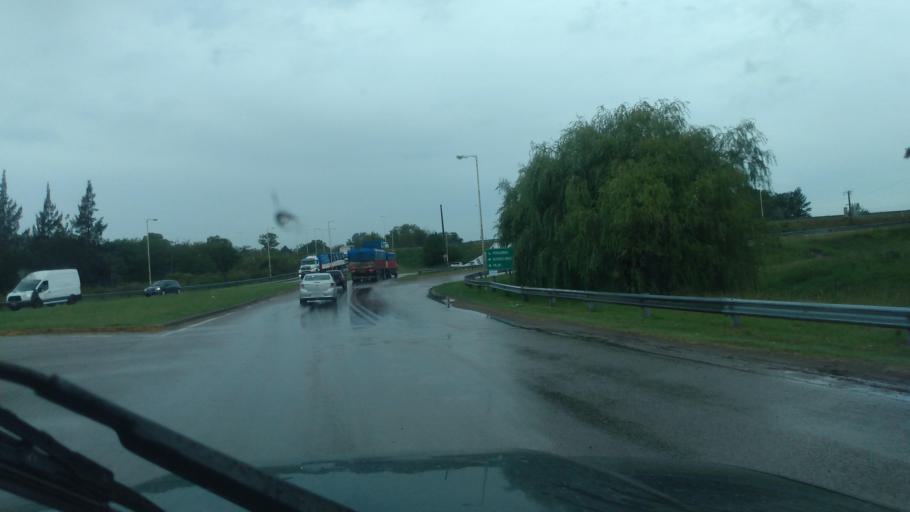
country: AR
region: Buenos Aires
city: Capilla del Senor
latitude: -34.3897
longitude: -59.0356
